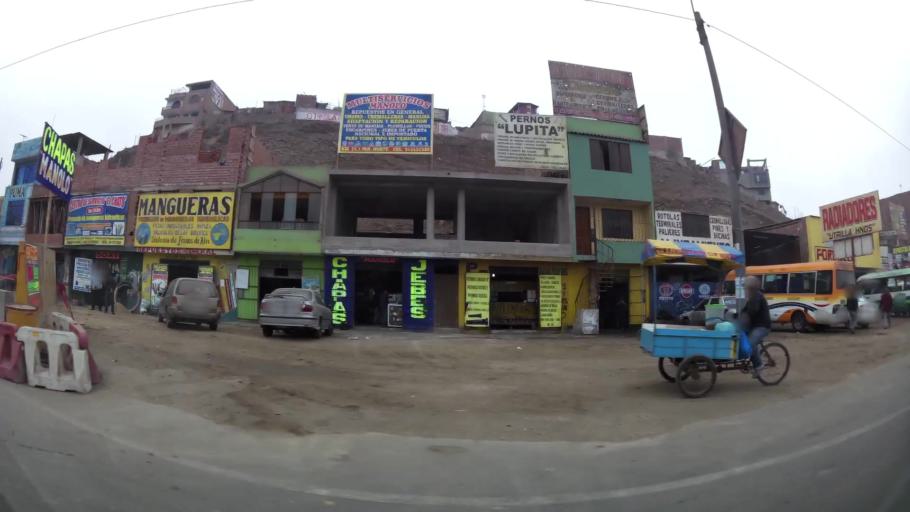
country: PE
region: Lima
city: Ventanilla
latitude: -11.8507
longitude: -77.0921
